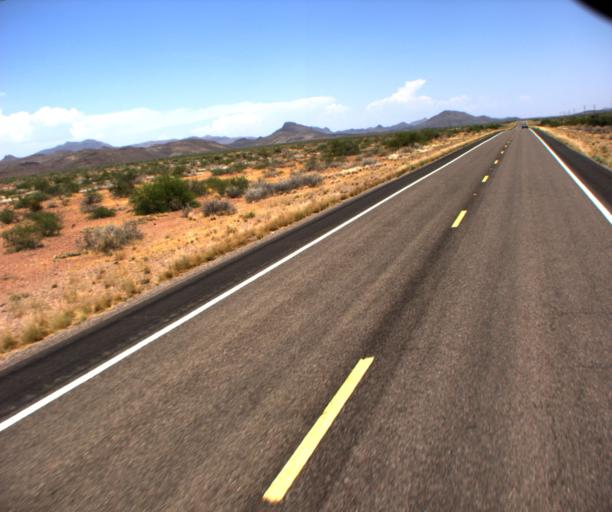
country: US
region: Arizona
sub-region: Graham County
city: Safford
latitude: 32.7693
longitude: -109.4748
